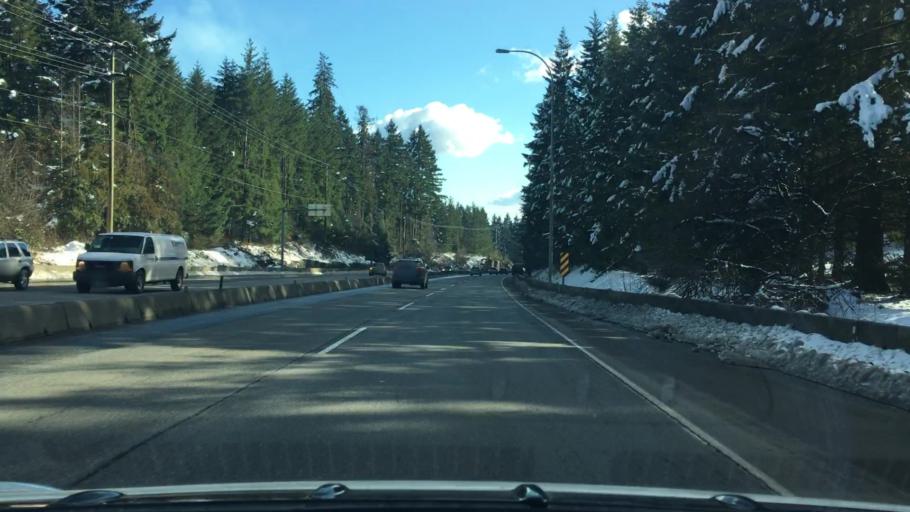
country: CA
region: British Columbia
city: Nanaimo
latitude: 49.0930
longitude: -123.8855
